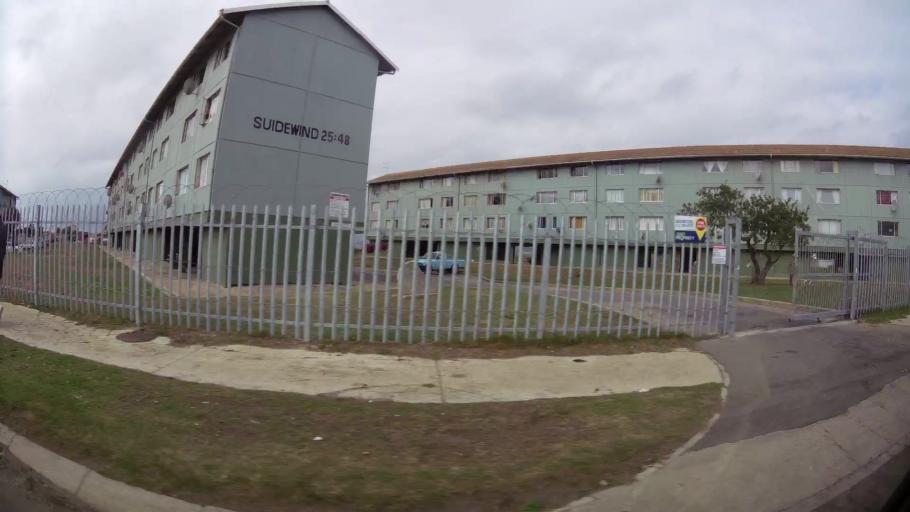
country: ZA
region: Eastern Cape
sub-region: Nelson Mandela Bay Metropolitan Municipality
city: Port Elizabeth
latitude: -33.8950
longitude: 25.5529
